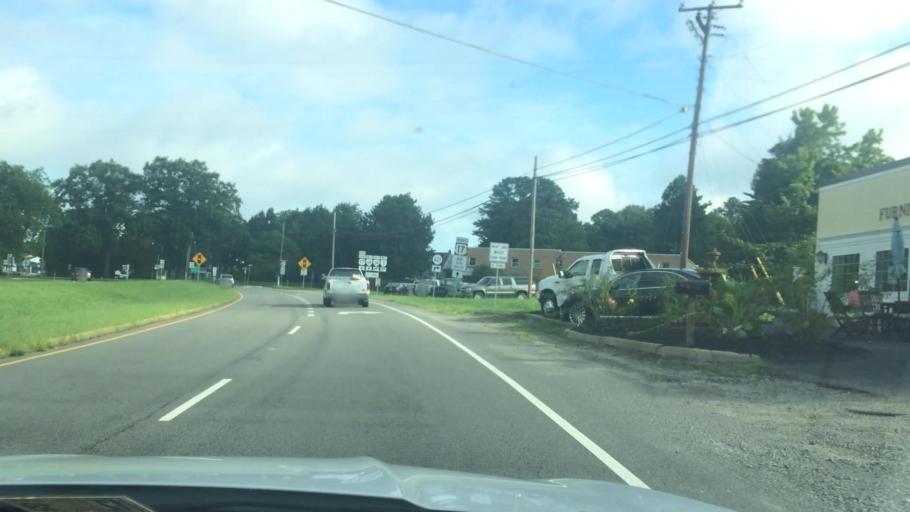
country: US
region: Virginia
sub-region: Gloucester County
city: Gloucester Courthouse
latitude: 37.4106
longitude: -76.5184
